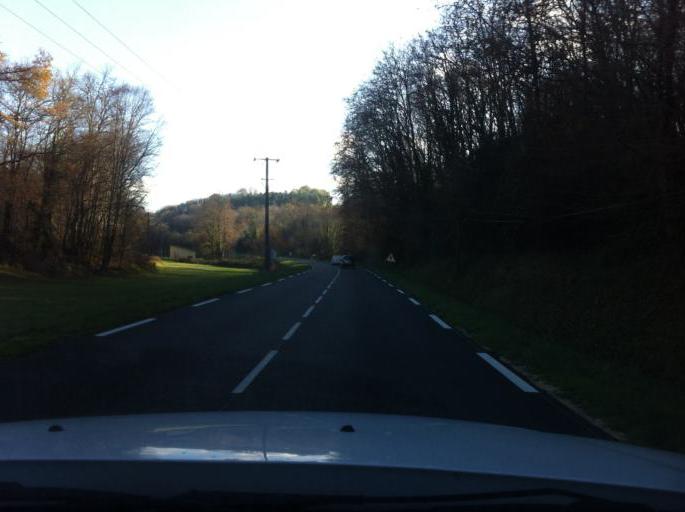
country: FR
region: Aquitaine
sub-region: Departement de la Dordogne
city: Rouffignac-Saint-Cernin-de-Reilhac
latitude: 45.0381
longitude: 0.8934
